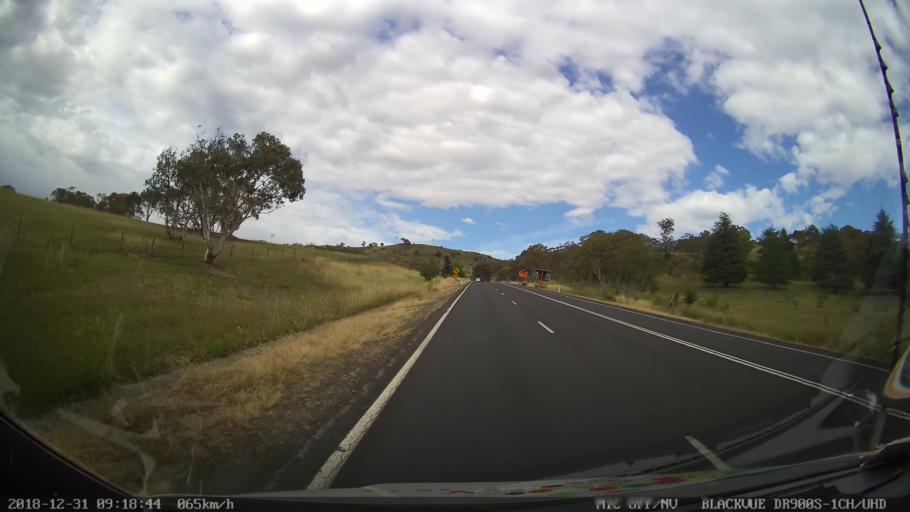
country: AU
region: New South Wales
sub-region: Snowy River
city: Jindabyne
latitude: -36.4106
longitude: 148.5912
